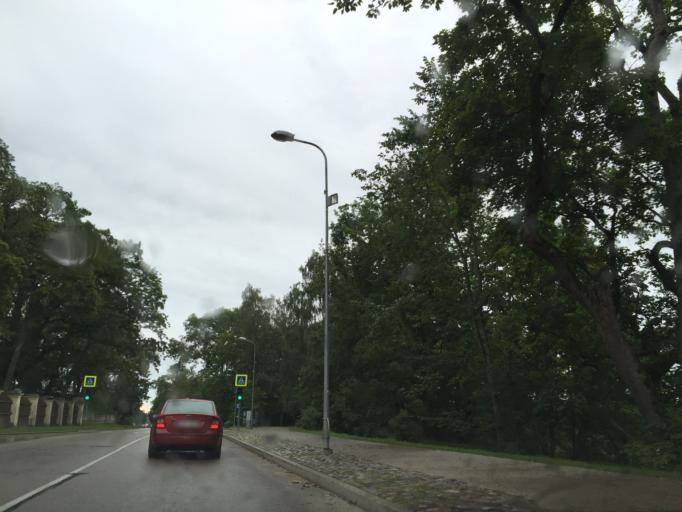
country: LV
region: Jekabpils Rajons
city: Jekabpils
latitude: 56.5109
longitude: 25.8586
